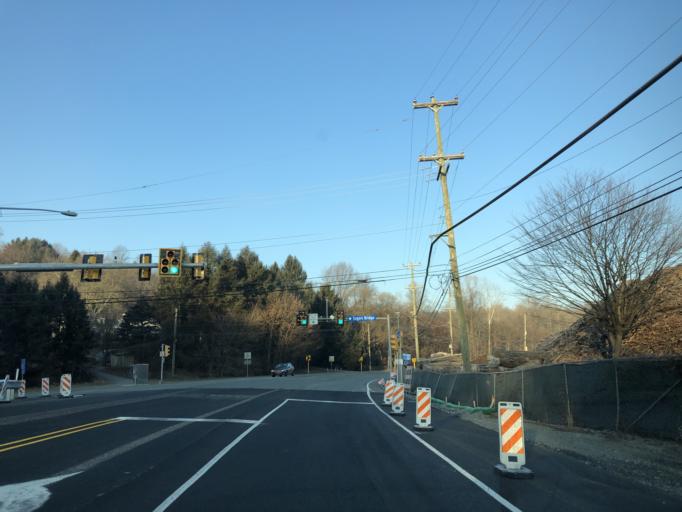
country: US
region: Pennsylvania
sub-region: Chester County
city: Downingtown
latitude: 39.9683
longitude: -75.6744
